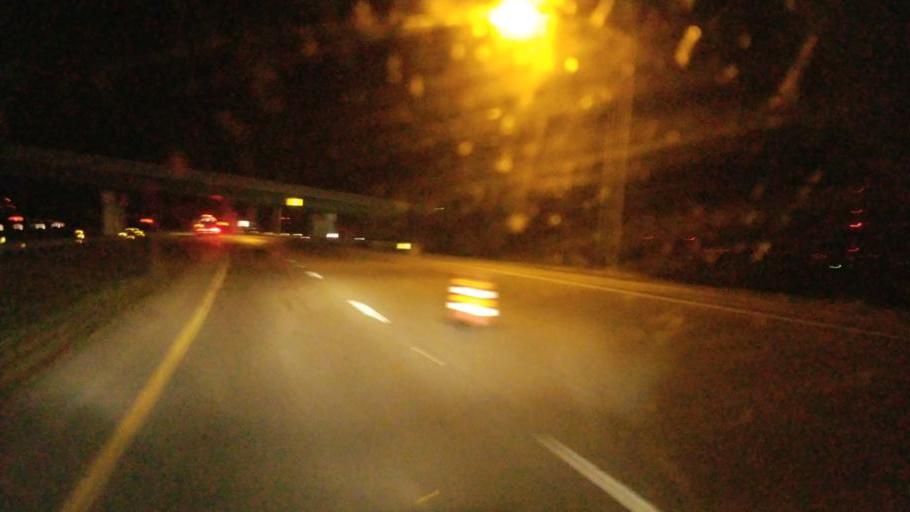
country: US
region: Ohio
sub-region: Van Wert County
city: Van Wert
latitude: 40.8825
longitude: -84.5280
